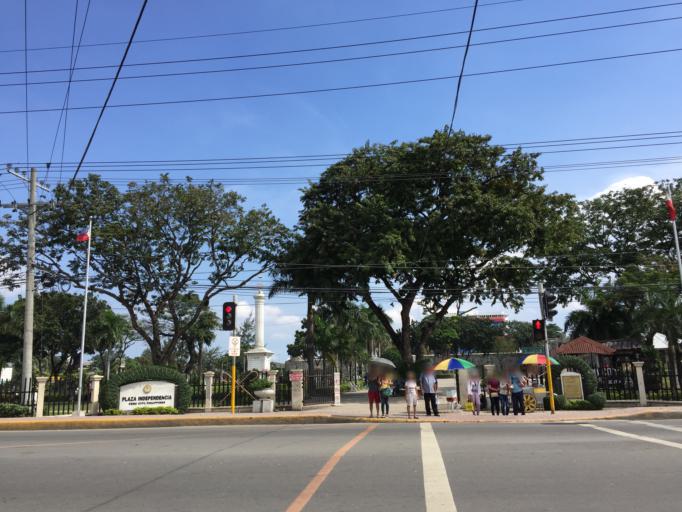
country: PH
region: Central Visayas
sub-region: Cebu City
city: Calero
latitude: 10.2935
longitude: 123.9045
